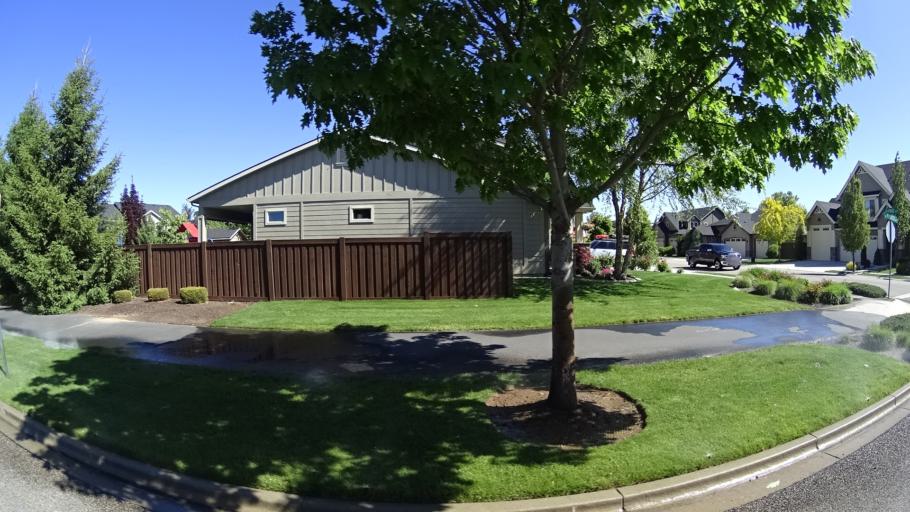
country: US
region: Idaho
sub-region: Ada County
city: Meridian
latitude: 43.6555
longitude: -116.3956
